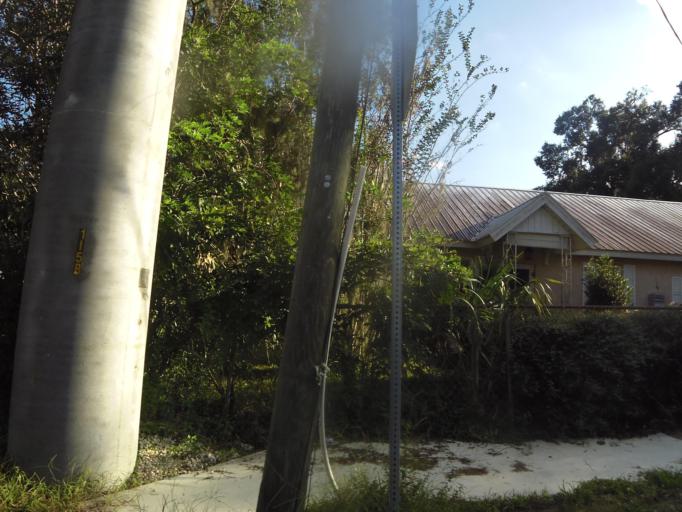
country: US
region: Florida
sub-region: Putnam County
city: Palatka
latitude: 29.6417
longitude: -81.6476
